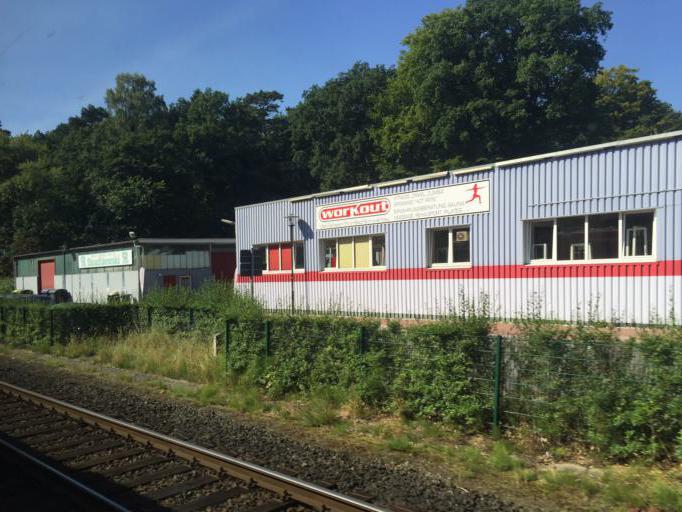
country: DE
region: Schleswig-Holstein
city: Bad Schwartau
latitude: 53.9190
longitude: 10.7058
